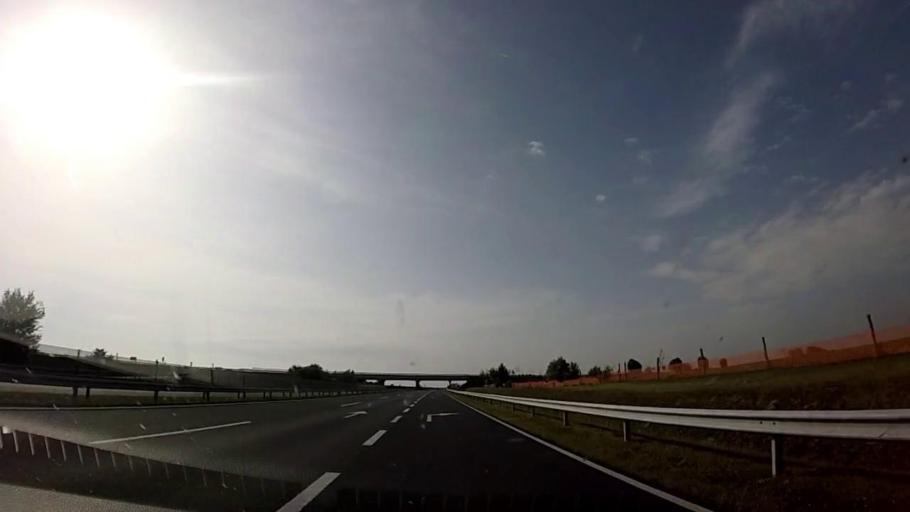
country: HU
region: Zala
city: Murakeresztur
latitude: 46.4603
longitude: 16.8891
